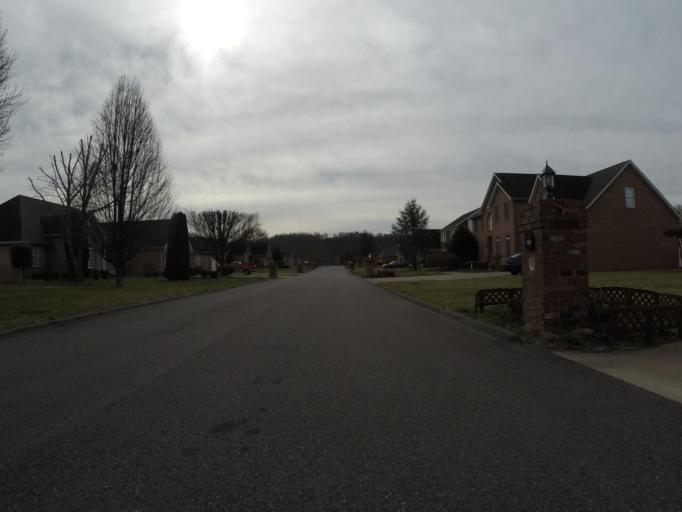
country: US
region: West Virginia
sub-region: Cabell County
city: Pea Ridge
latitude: 38.4456
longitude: -82.3486
